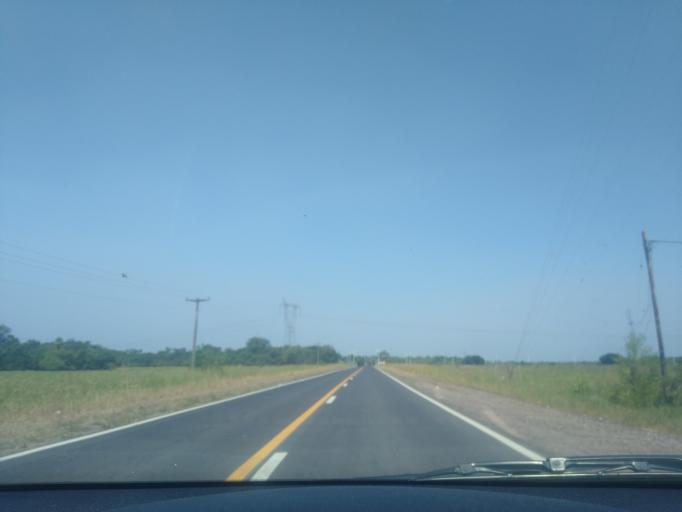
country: AR
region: Chaco
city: Fontana
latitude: -27.5767
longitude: -59.1629
